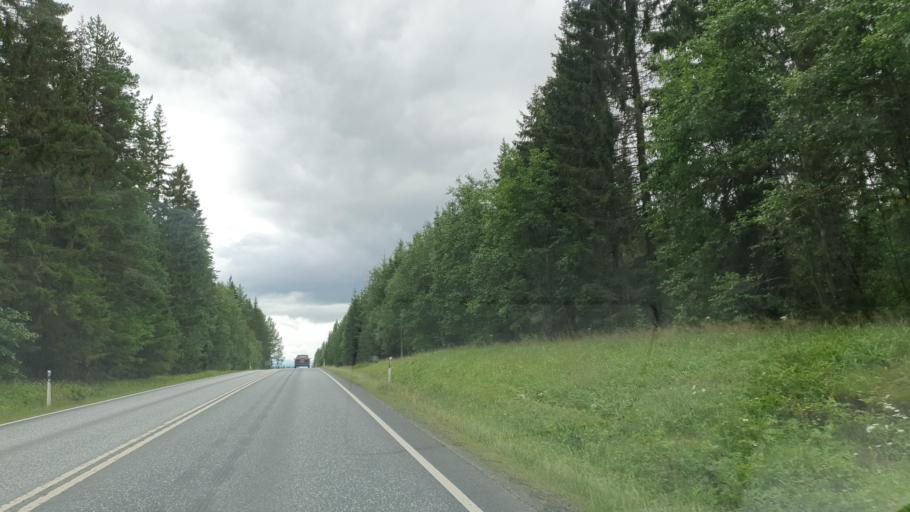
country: FI
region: Northern Savo
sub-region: Ylae-Savo
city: Sonkajaervi
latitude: 63.7814
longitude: 27.4165
